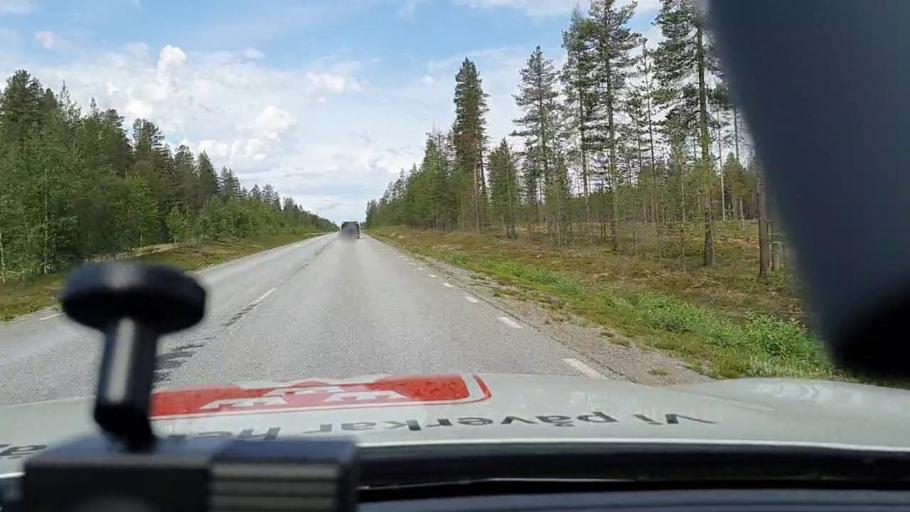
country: SE
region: Norrbotten
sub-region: Jokkmokks Kommun
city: Jokkmokk
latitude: 66.5225
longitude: 20.2076
